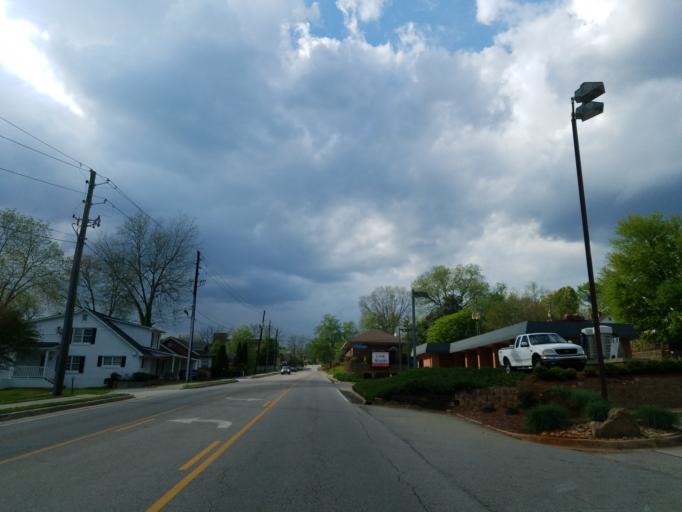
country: US
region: Georgia
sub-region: Lumpkin County
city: Dahlonega
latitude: 34.5291
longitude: -83.9818
